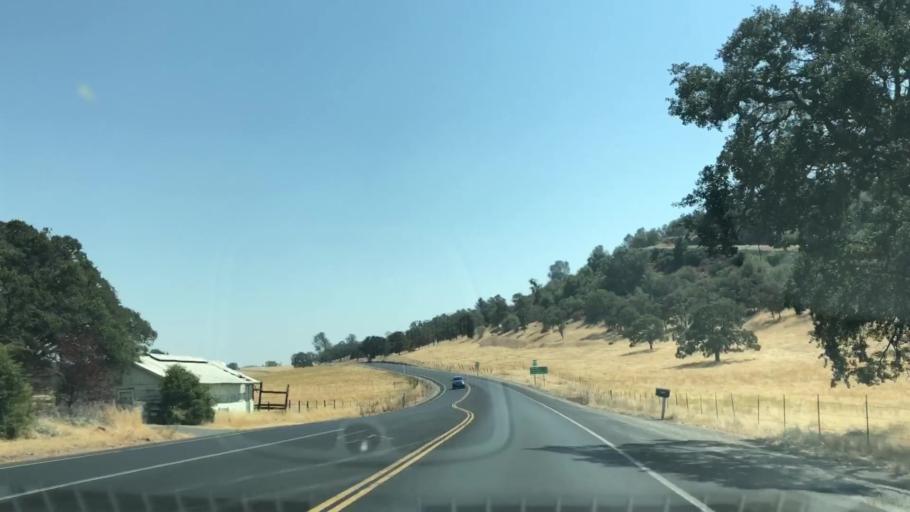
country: US
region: California
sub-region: Tuolumne County
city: Jamestown
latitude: 37.8876
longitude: -120.4860
